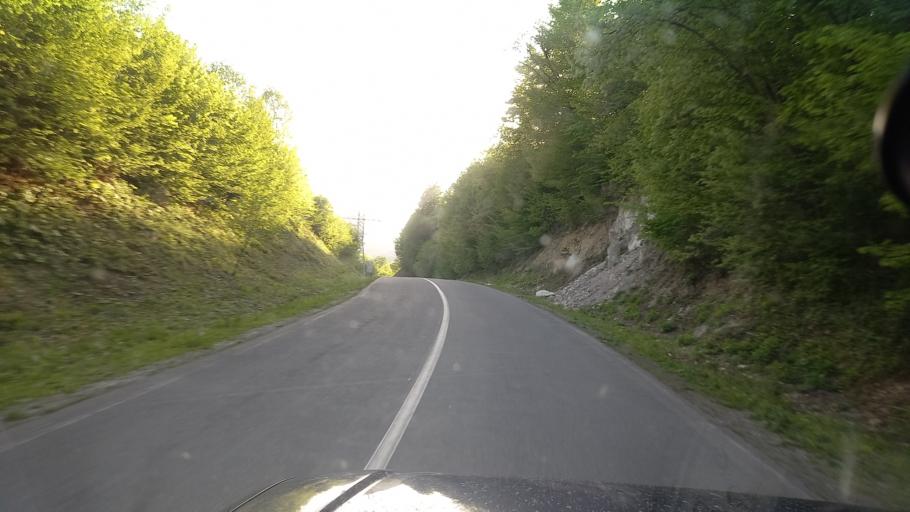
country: RU
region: Ingushetiya
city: Galashki
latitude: 42.9075
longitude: 44.9801
